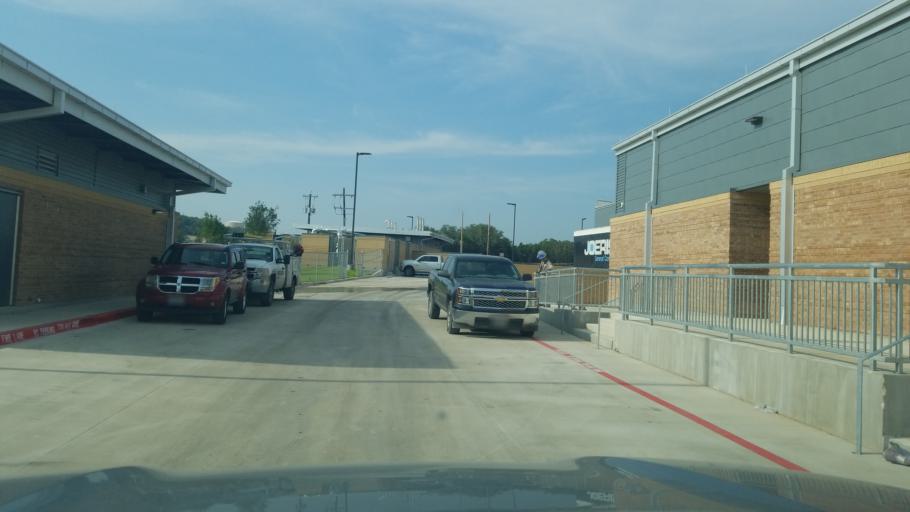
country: US
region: Texas
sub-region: Bexar County
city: Timberwood Park
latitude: 29.7176
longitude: -98.4695
